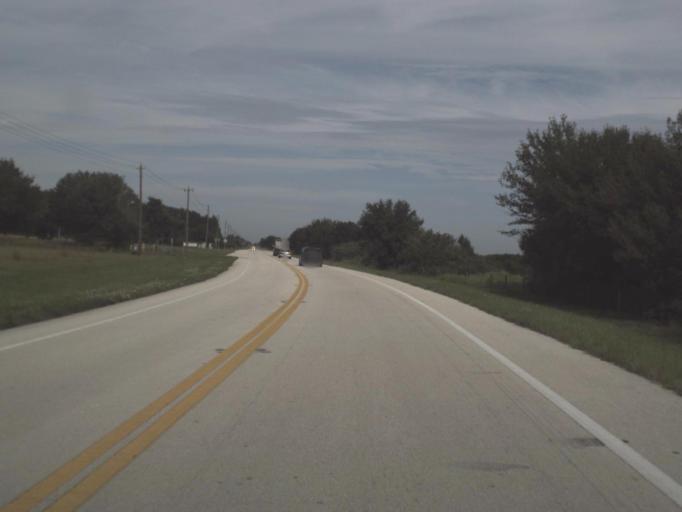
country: US
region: Florida
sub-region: DeSoto County
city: Southeast Arcadia
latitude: 27.1395
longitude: -81.7970
